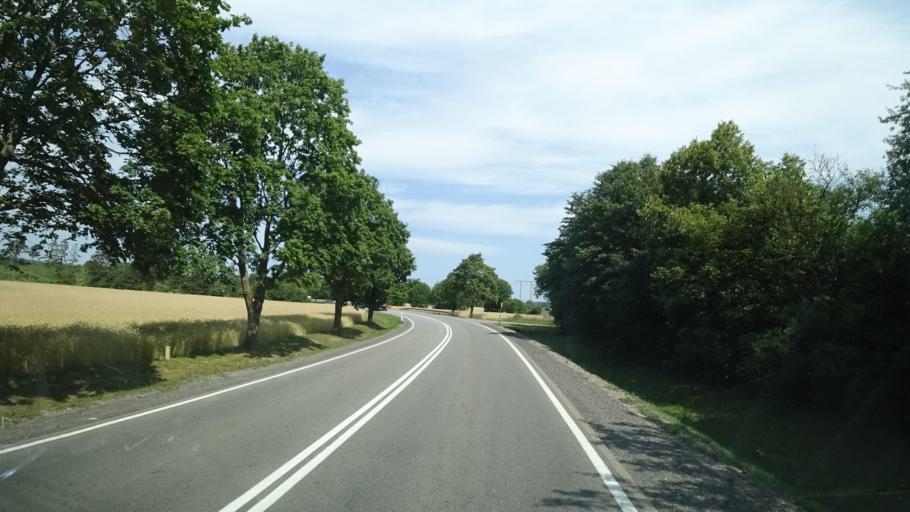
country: PL
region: Pomeranian Voivodeship
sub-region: Powiat kartuski
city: Banino
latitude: 54.3400
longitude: 18.4410
